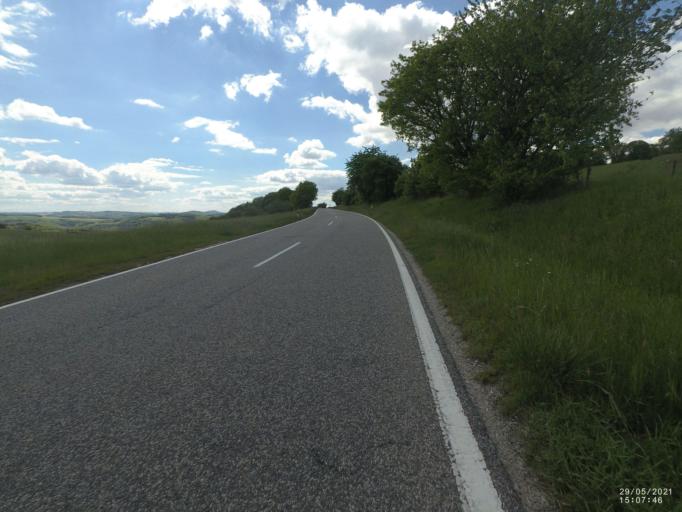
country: DE
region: Rheinland-Pfalz
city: Brodenbach
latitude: 50.2362
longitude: 7.4662
